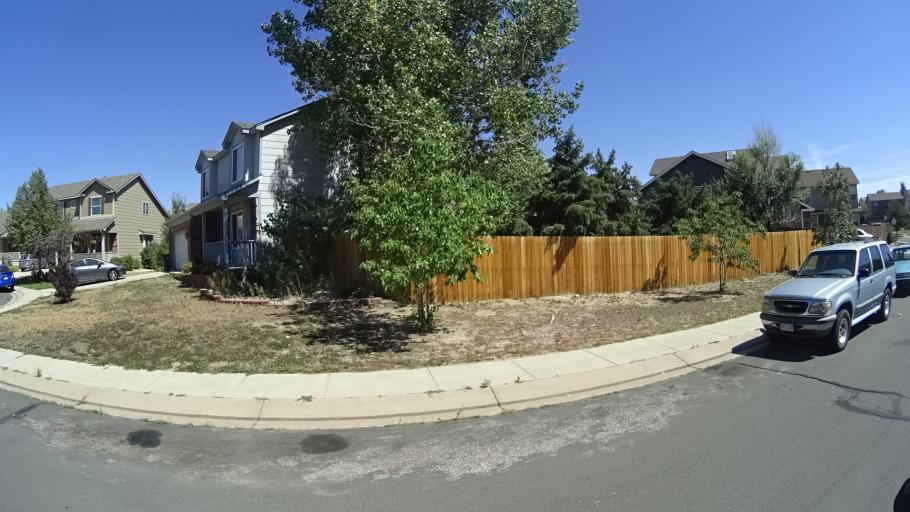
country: US
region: Colorado
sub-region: El Paso County
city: Black Forest
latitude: 38.9502
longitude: -104.7602
